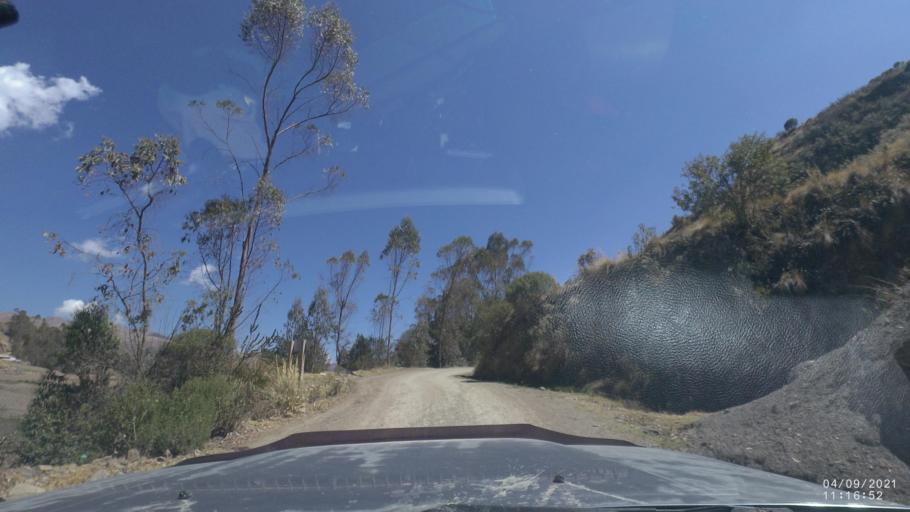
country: BO
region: Cochabamba
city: Sipe Sipe
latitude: -17.2709
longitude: -66.4849
